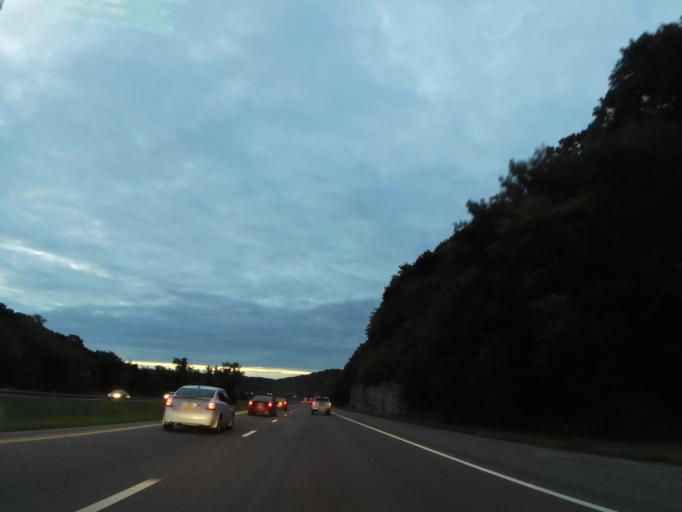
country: US
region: Tennessee
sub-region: Davidson County
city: Goodlettsville
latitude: 36.2664
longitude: -86.7915
